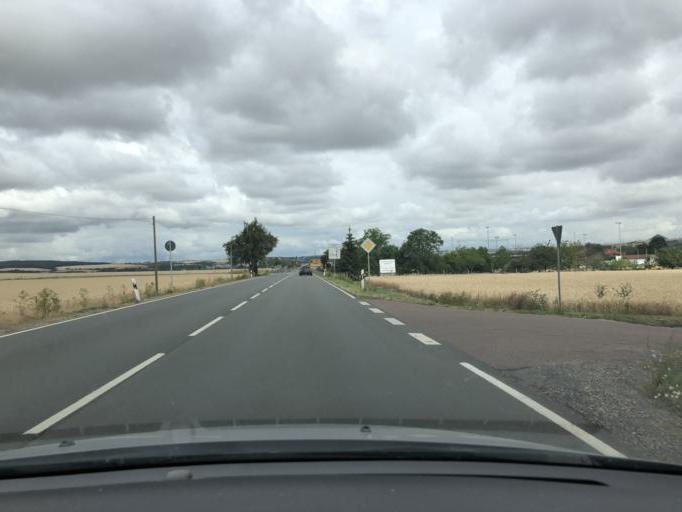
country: DE
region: Saxony-Anhalt
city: Erdeborn
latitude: 51.4976
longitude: 11.6322
